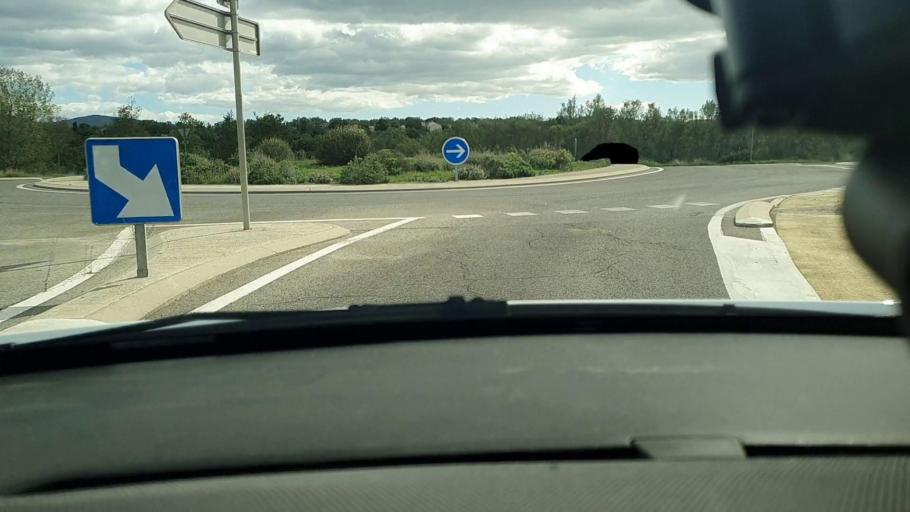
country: FR
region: Languedoc-Roussillon
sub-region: Departement du Gard
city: Salindres
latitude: 44.1910
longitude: 4.2176
